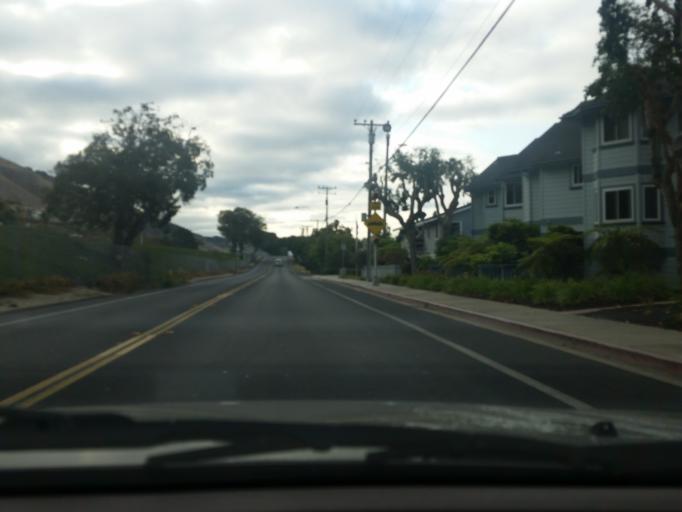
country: US
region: California
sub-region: San Luis Obispo County
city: Pismo Beach
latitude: 35.1627
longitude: -120.6852
